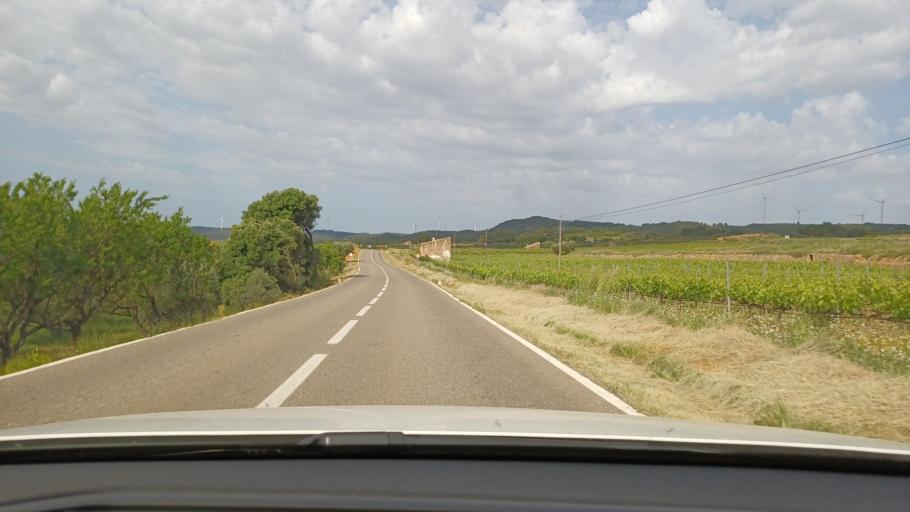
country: ES
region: Catalonia
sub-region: Provincia de Tarragona
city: Bot
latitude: 41.0423
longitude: 0.3902
